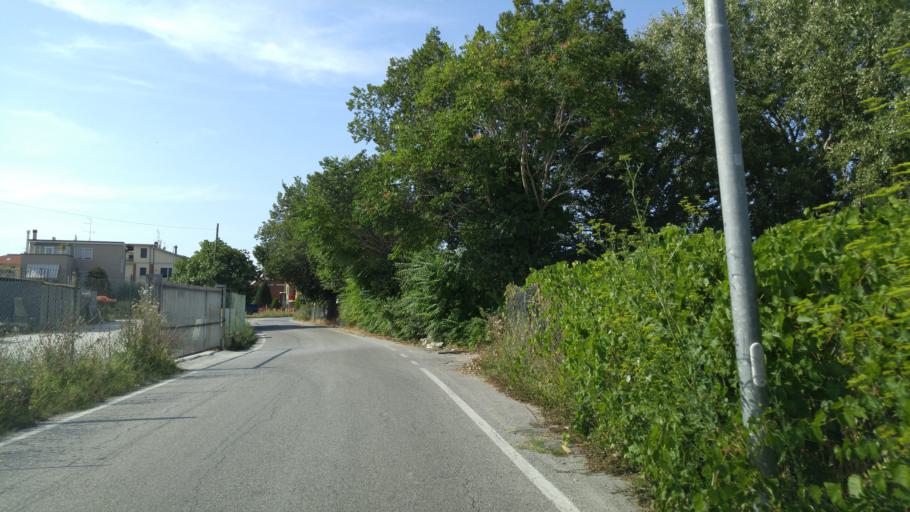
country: IT
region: The Marches
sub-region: Provincia di Pesaro e Urbino
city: Pesaro
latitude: 43.9004
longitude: 12.9140
